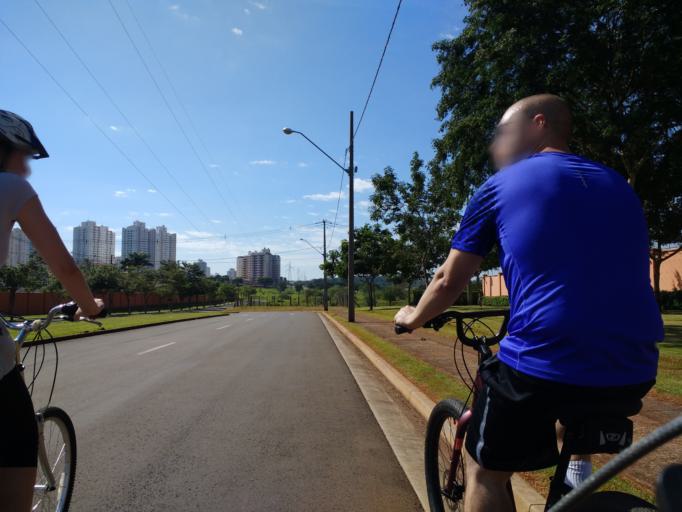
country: BR
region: Parana
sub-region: Londrina
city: Londrina
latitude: -23.3529
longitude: -51.1862
